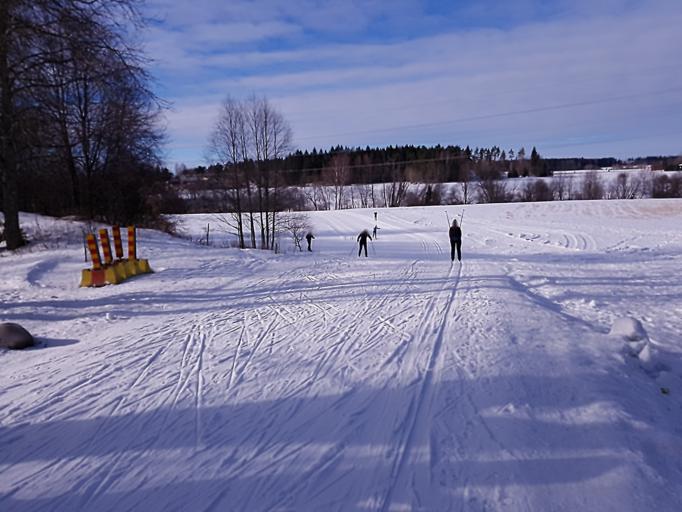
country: FI
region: Uusimaa
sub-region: Helsinki
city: Helsinki
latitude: 60.2743
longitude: 24.9375
